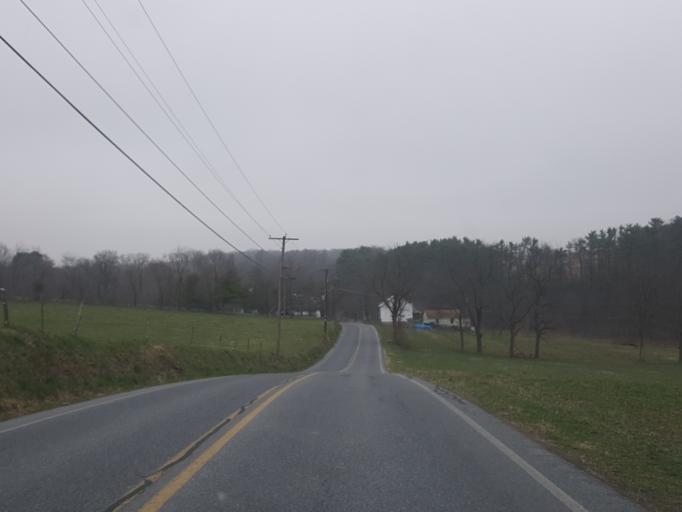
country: US
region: Pennsylvania
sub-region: Schuylkill County
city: Pine Grove
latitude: 40.5439
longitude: -76.4635
